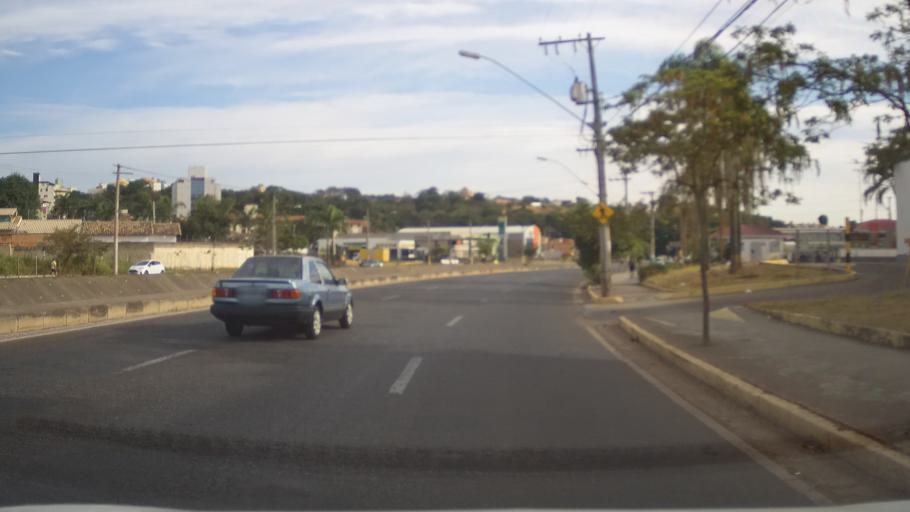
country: BR
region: Minas Gerais
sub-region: Contagem
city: Contagem
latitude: -19.8795
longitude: -44.0056
